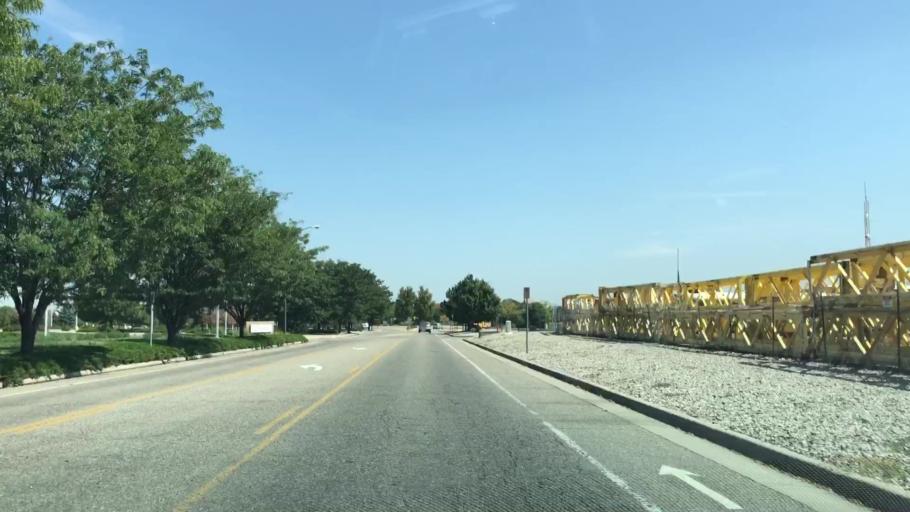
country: US
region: Colorado
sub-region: Larimer County
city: Loveland
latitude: 40.4052
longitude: -105.0425
